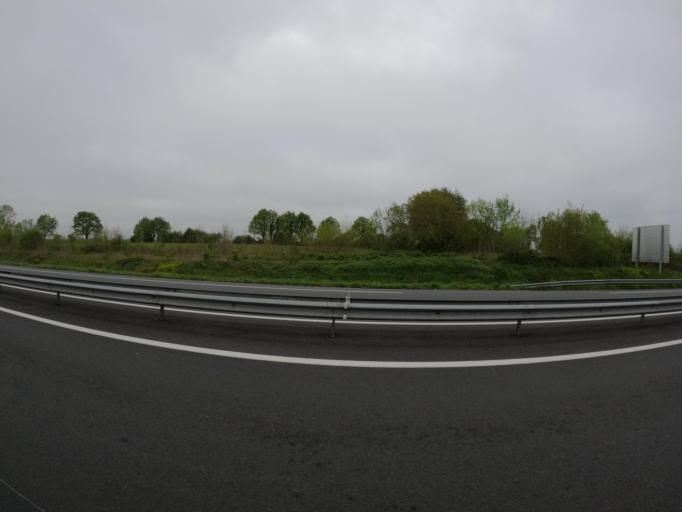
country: FR
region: Pays de la Loire
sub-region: Departement de la Vendee
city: Saint-Fulgent
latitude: 46.8460
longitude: -1.1477
